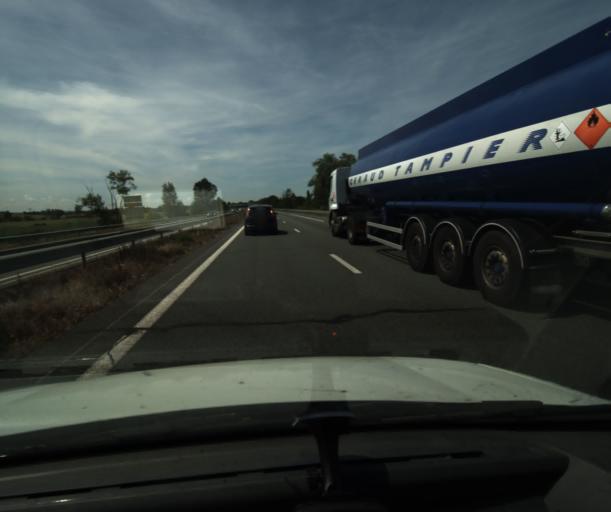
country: FR
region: Languedoc-Roussillon
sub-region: Departement de l'Aude
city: Bram
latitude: 43.2327
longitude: 2.1068
